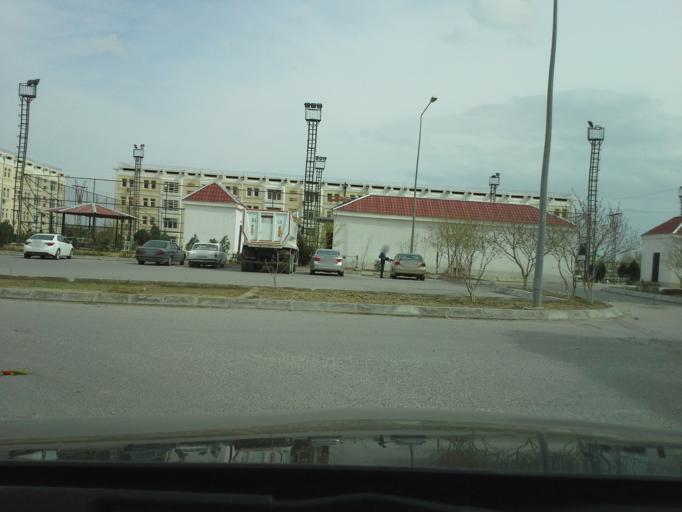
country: TM
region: Ahal
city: Abadan
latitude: 38.0556
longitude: 58.1433
